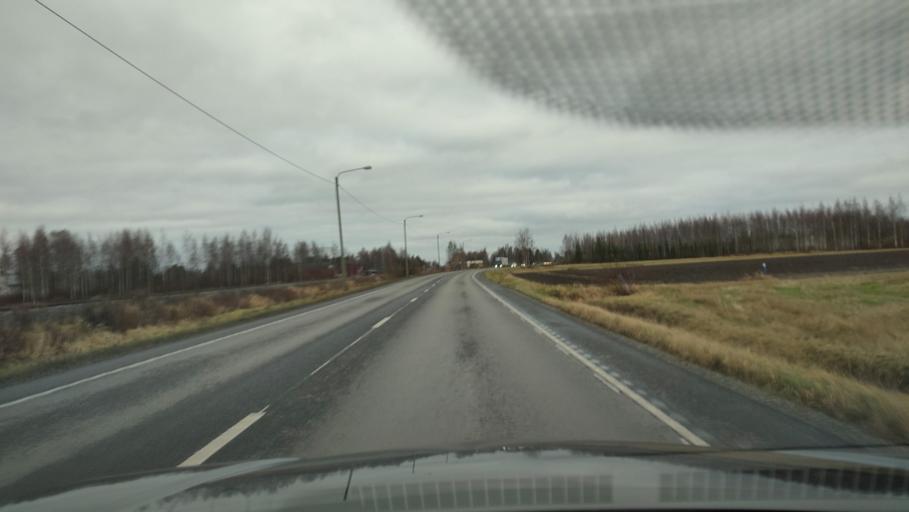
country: FI
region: Southern Ostrobothnia
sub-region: Seinaejoki
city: Ilmajoki
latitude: 62.7238
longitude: 22.5739
